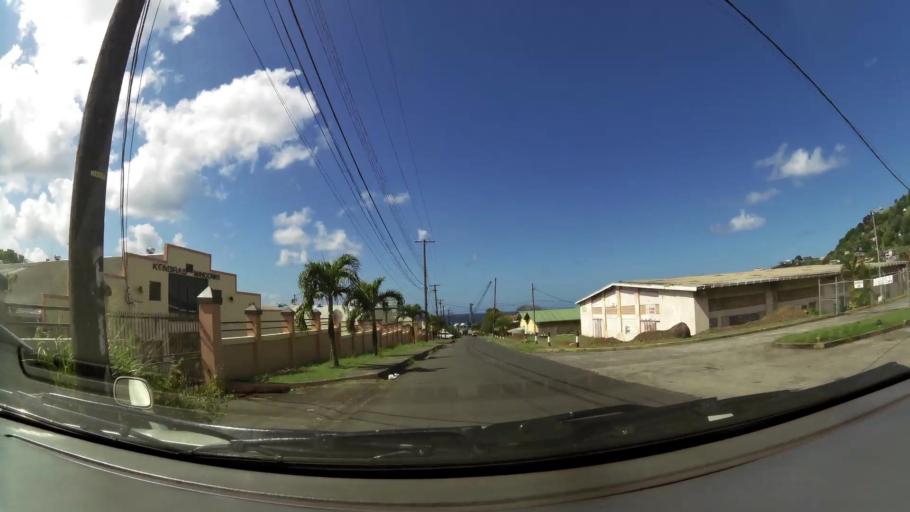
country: VC
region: Saint George
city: Kingstown Park
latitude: 13.1706
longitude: -61.2438
